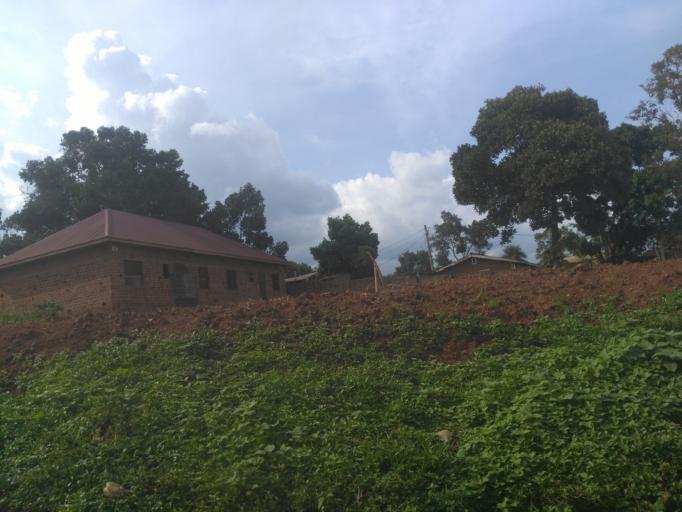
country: UG
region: Central Region
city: Kampala Central Division
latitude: 0.3639
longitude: 32.5565
